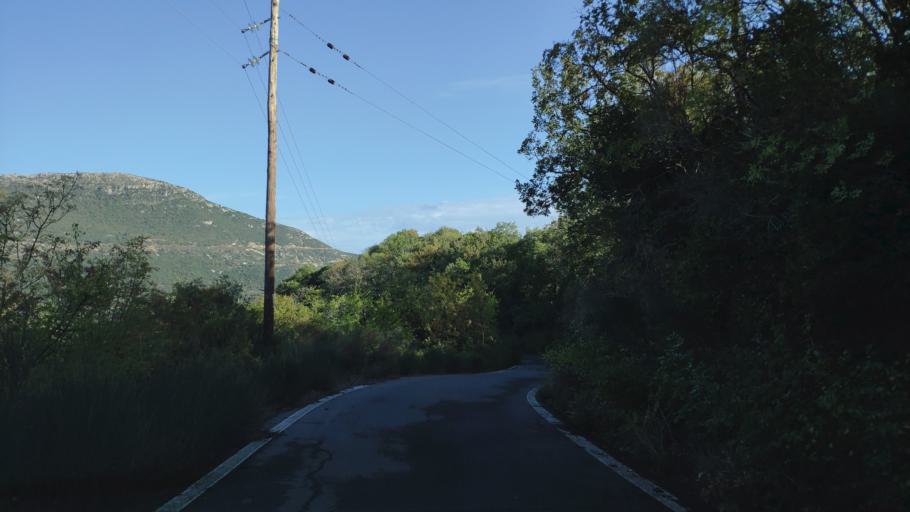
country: GR
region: Peloponnese
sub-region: Nomos Arkadias
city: Dimitsana
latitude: 37.5591
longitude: 22.0365
